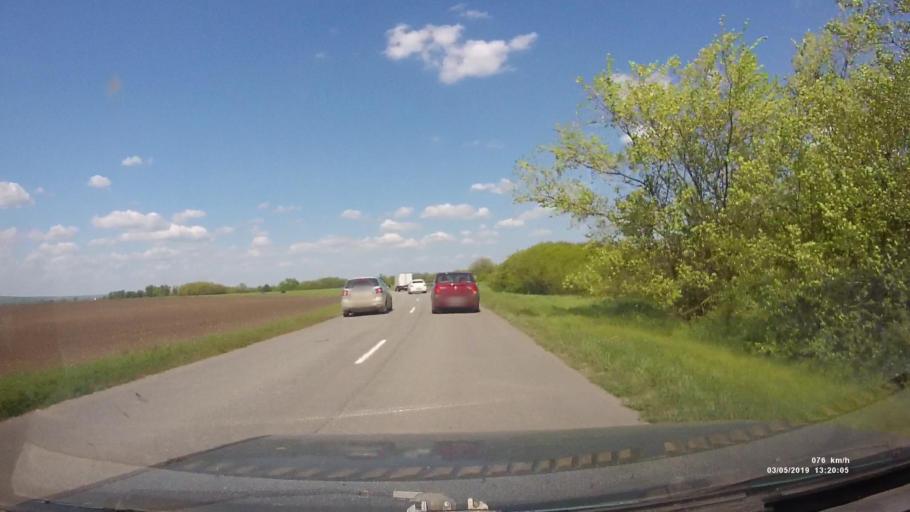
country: RU
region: Rostov
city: Semikarakorsk
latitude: 47.5428
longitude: 40.7538
